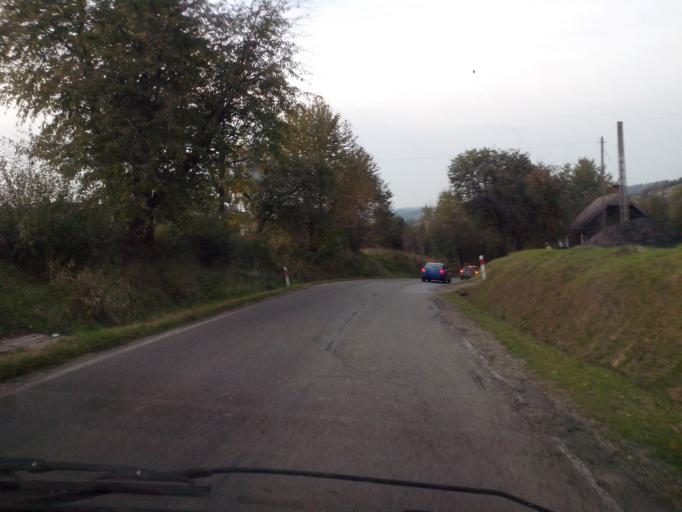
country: PL
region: Subcarpathian Voivodeship
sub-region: Powiat strzyzowski
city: Strzyzow
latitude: 49.8204
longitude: 21.8338
